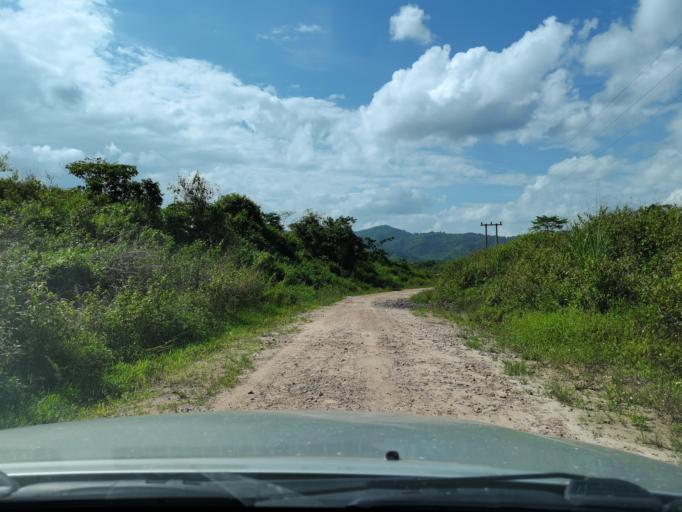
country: LA
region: Loungnamtha
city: Muang Nale
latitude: 20.5835
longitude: 101.0595
